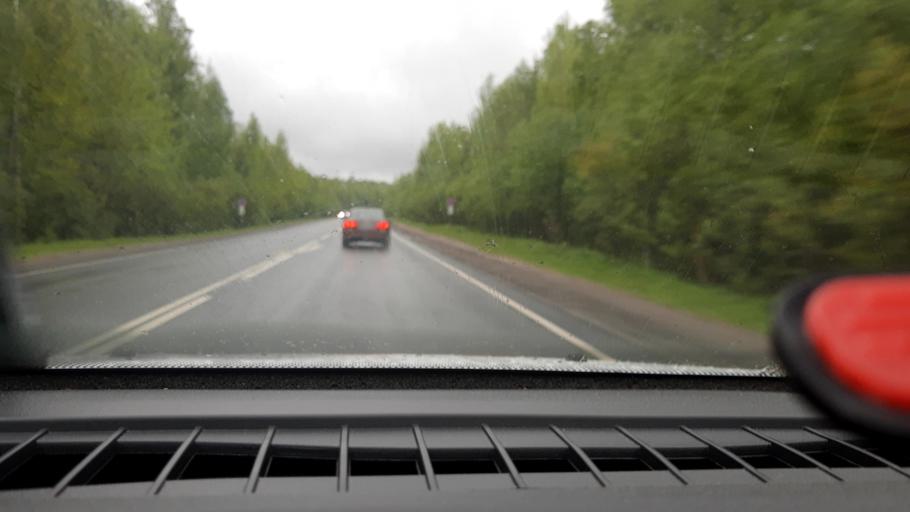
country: RU
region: Nizjnij Novgorod
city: Semenov
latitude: 56.7522
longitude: 44.3608
